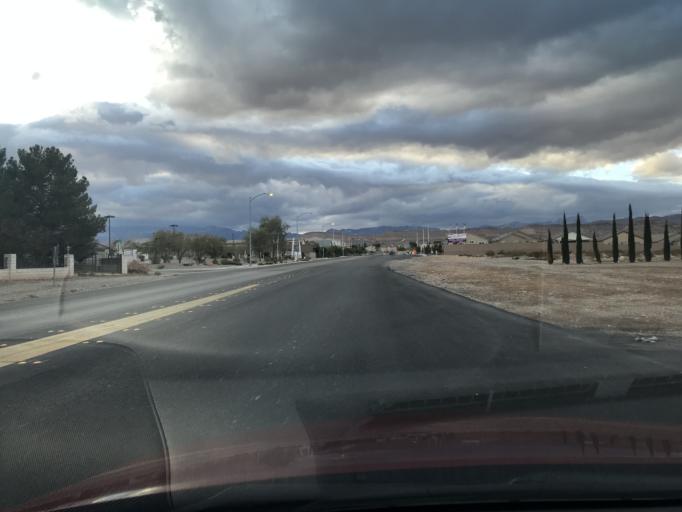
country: US
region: Nevada
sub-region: Clark County
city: Enterprise
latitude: 36.0403
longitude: -115.2741
